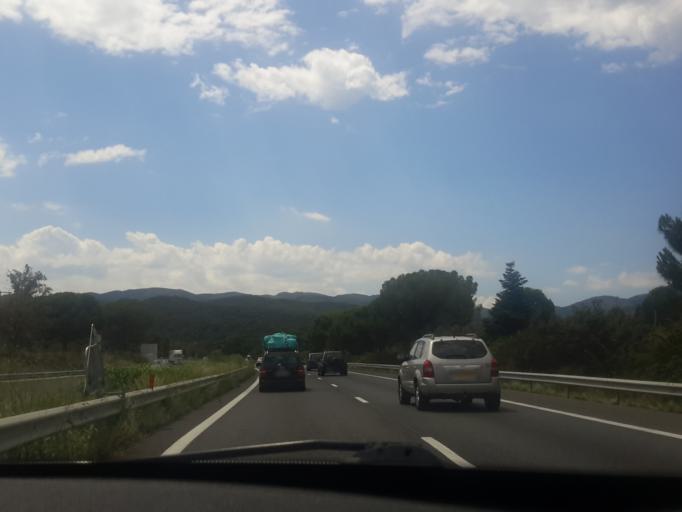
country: FR
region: Languedoc-Roussillon
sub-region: Departement des Pyrenees-Orientales
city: Maureillas-las-Illas
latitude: 42.5055
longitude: 2.8180
